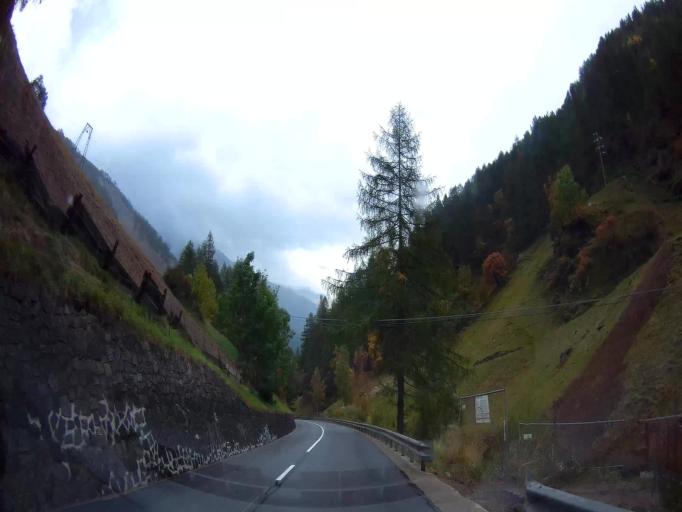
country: IT
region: Trentino-Alto Adige
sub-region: Bolzano
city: Senales
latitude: 46.7140
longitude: 10.8866
